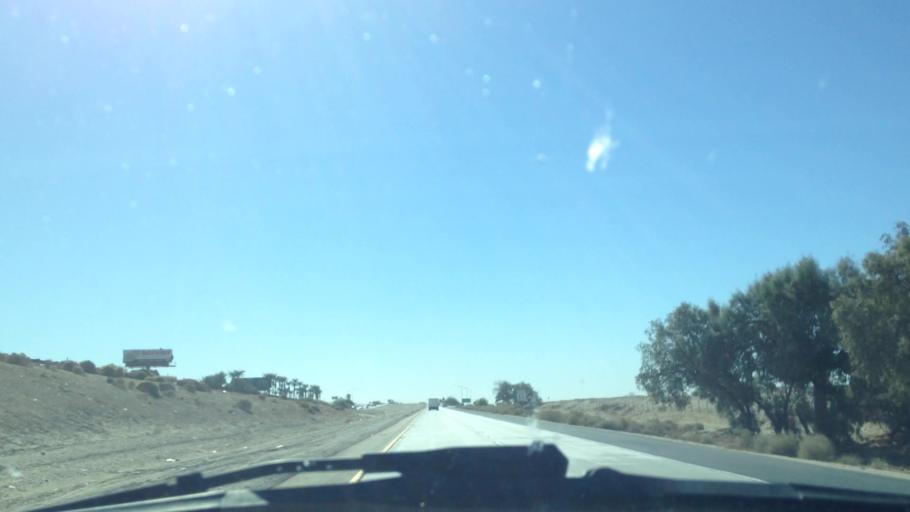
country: US
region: California
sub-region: Riverside County
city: Indio
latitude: 33.7143
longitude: -116.1894
